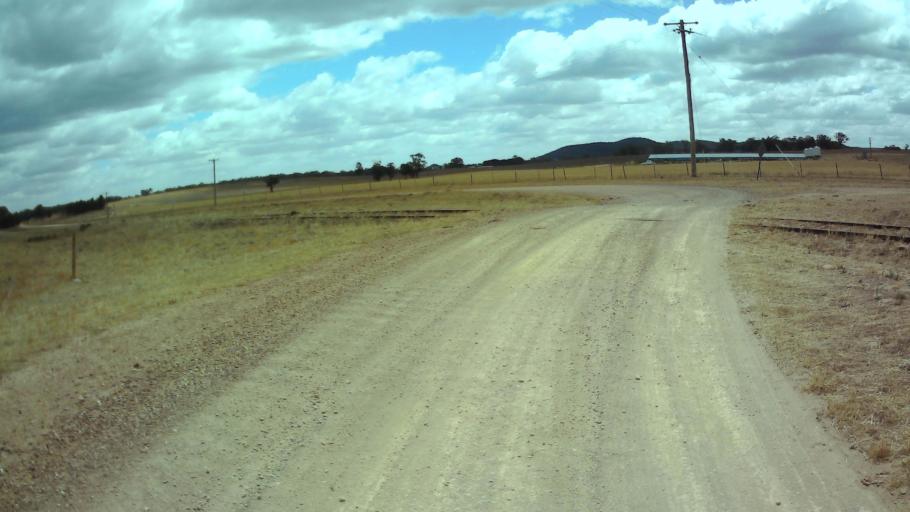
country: AU
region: New South Wales
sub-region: Weddin
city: Grenfell
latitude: -33.9371
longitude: 148.2856
